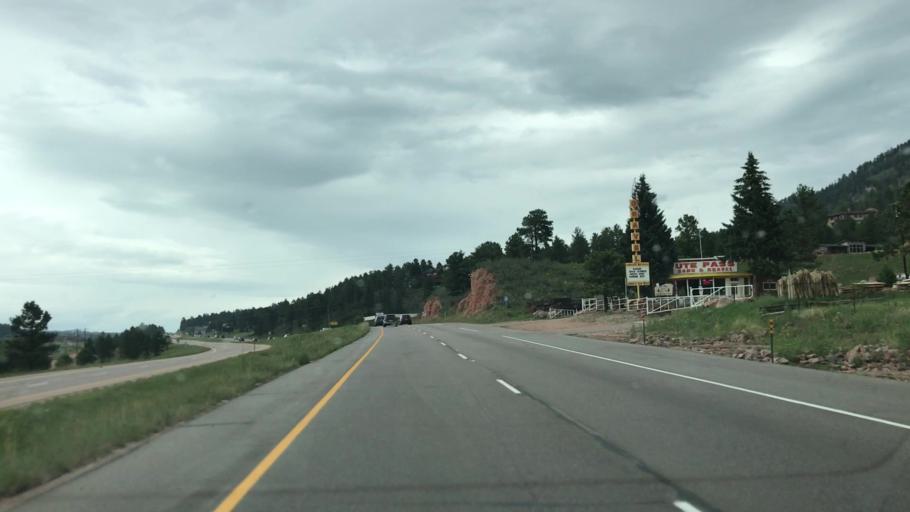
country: US
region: Colorado
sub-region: El Paso County
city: Cascade-Chipita Park
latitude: 38.9603
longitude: -105.0289
